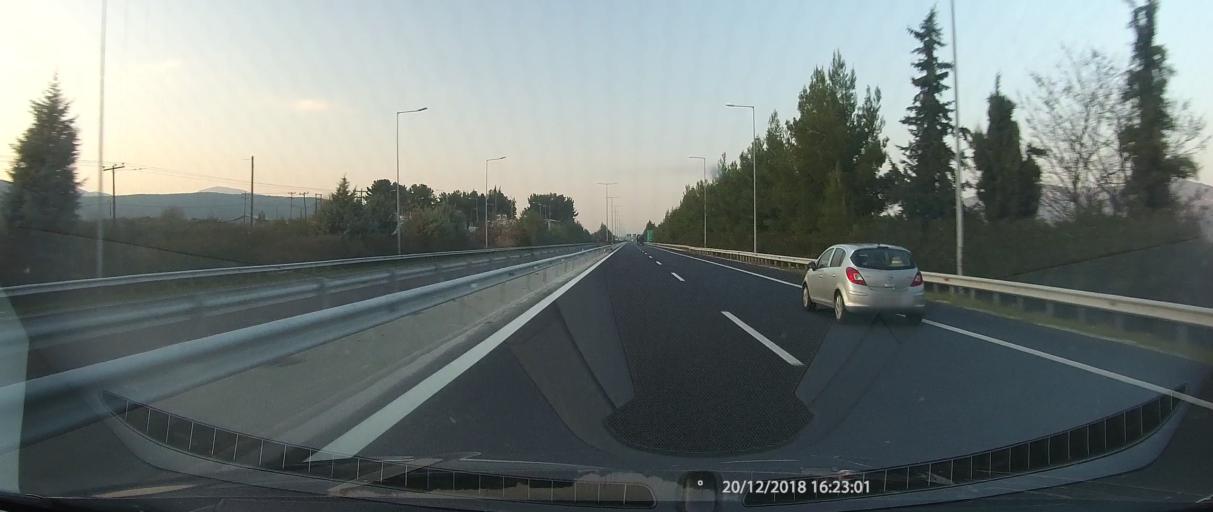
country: GR
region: Thessaly
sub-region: Nomos Magnisias
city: Sourpi
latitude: 39.0818
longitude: 22.8789
